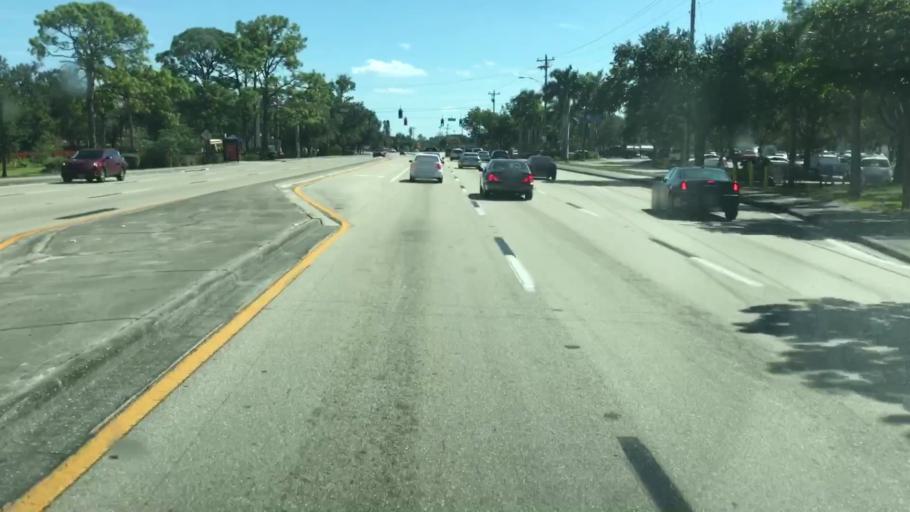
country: US
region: Florida
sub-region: Lee County
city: Lehigh Acres
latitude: 26.6164
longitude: -81.6664
